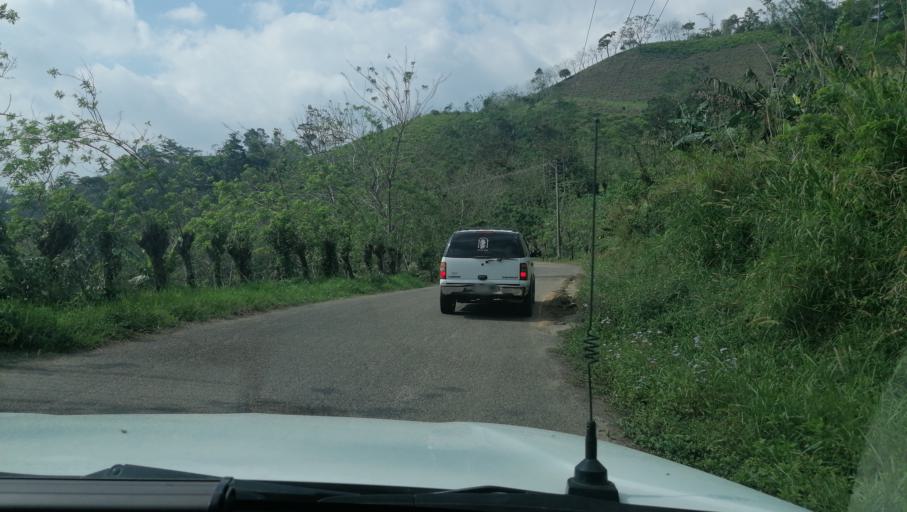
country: MX
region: Chiapas
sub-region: Francisco Leon
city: San Miguel la Sardina
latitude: 17.2333
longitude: -93.3346
